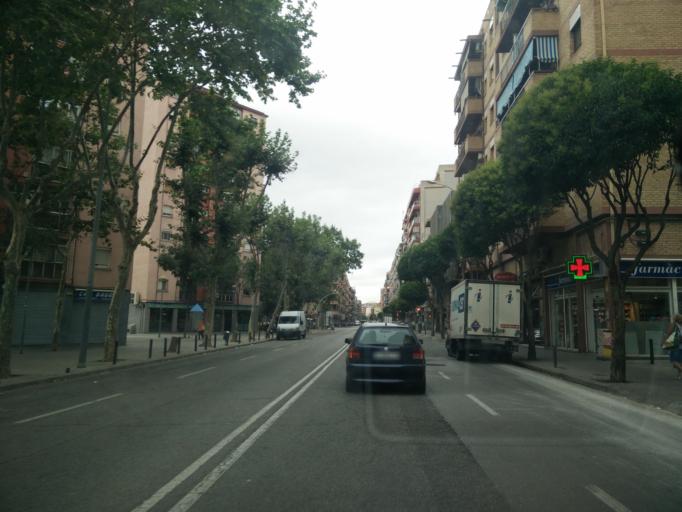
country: ES
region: Catalonia
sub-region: Provincia de Barcelona
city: Llefia
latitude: 41.4362
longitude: 2.2221
